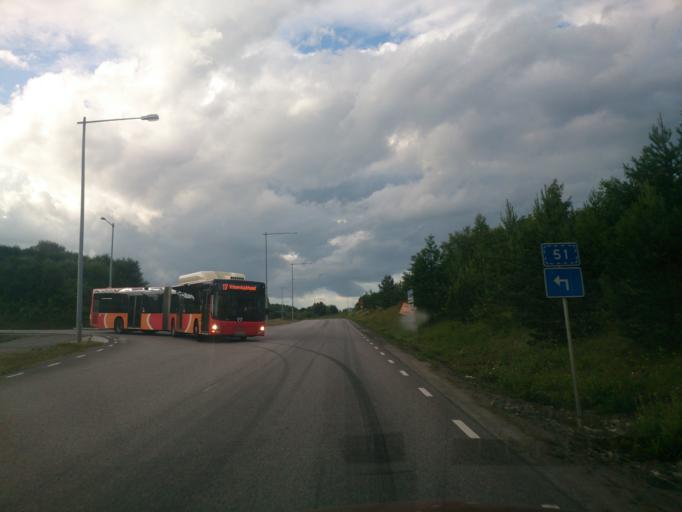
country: SE
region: OEstergoetland
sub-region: Norrkopings Kommun
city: Norrkoping
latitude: 58.6271
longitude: 16.1568
